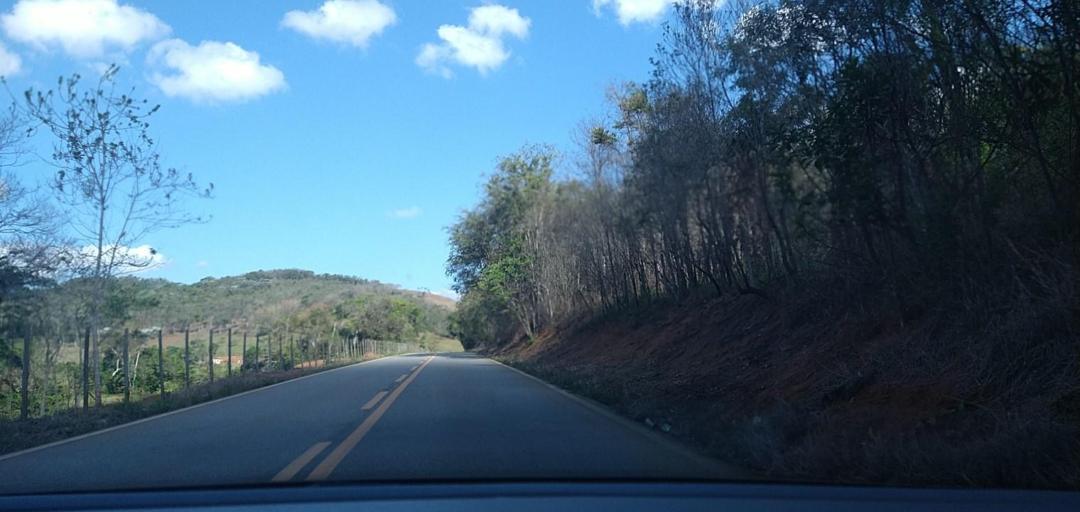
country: BR
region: Minas Gerais
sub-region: Alvinopolis
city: Alvinopolis
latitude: -20.0295
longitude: -43.0508
